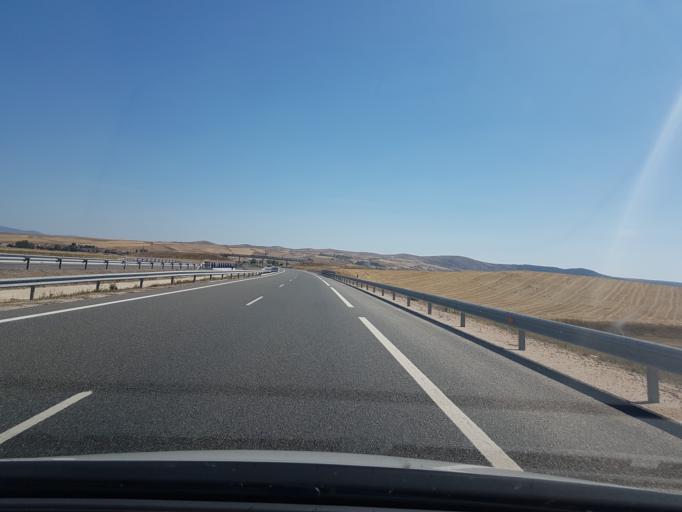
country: ES
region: Castille and Leon
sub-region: Provincia de Avila
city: Monsalupe
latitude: 40.8034
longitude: -4.7856
